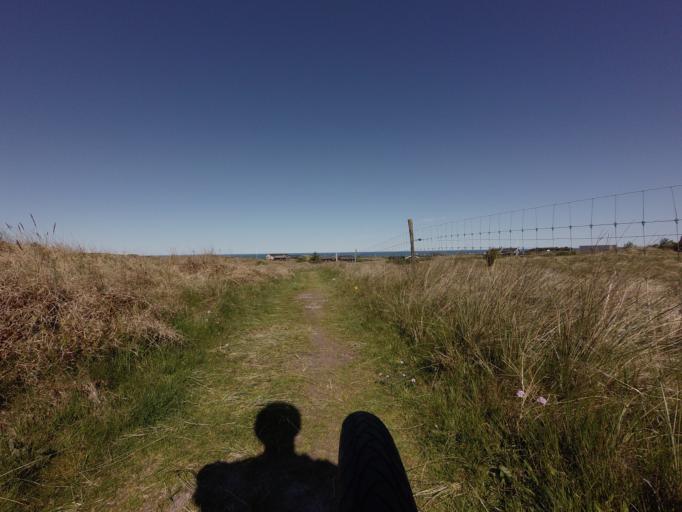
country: DK
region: North Denmark
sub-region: Jammerbugt Kommune
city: Pandrup
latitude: 57.3128
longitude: 9.6602
